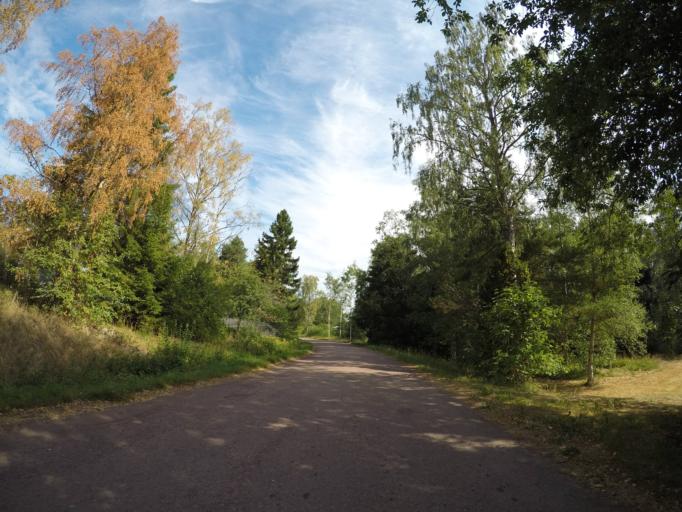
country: AX
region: Alands landsbygd
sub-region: Finstroem
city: Finstroem
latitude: 60.2079
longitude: 19.8750
